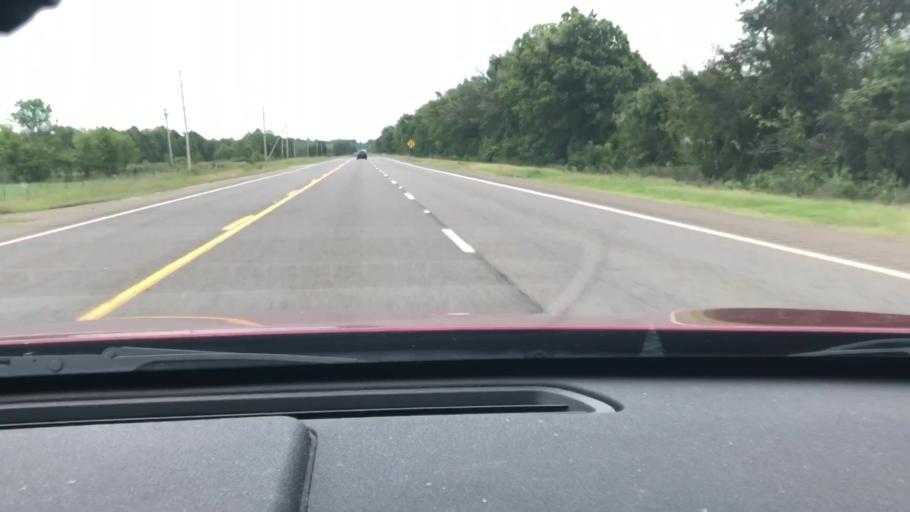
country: US
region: Arkansas
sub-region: Lafayette County
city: Lewisville
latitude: 33.3568
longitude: -93.6475
